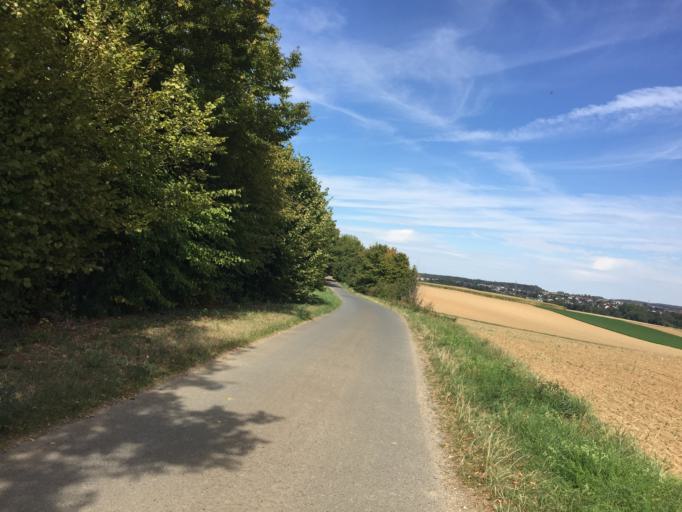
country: DE
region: Hesse
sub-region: Regierungsbezirk Giessen
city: Langgons
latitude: 50.4793
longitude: 8.6567
